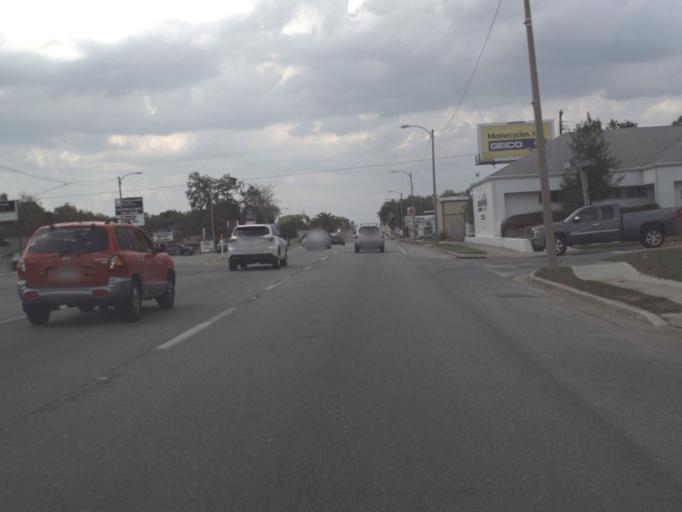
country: US
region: Florida
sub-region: Lake County
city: Eustis
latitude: 28.8312
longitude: -81.6854
